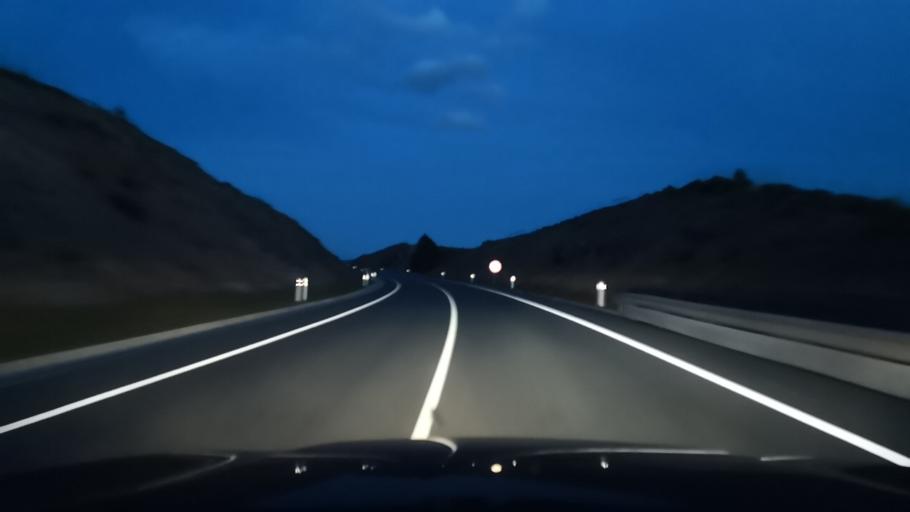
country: PT
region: Braganca
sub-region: Mogadouro
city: Mogadouro
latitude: 41.2550
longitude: -6.8201
